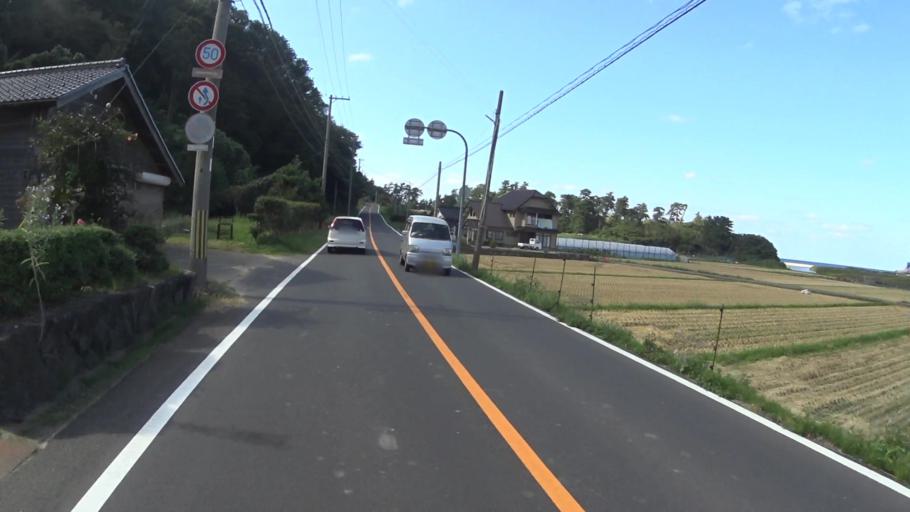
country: JP
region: Kyoto
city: Miyazu
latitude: 35.7489
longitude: 135.1611
